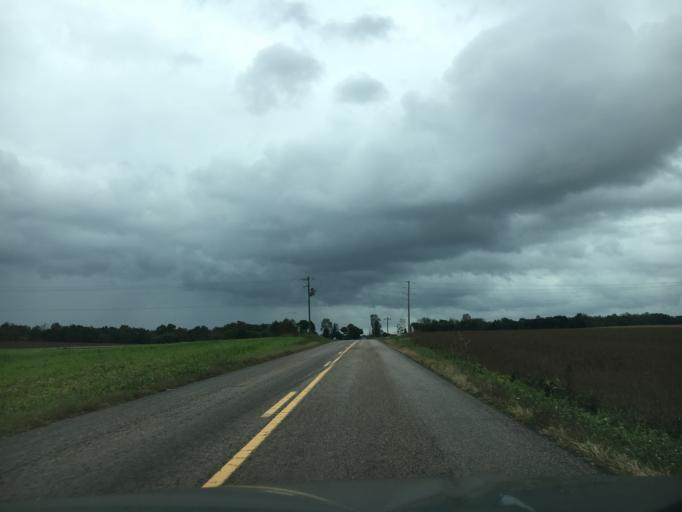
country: US
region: Virginia
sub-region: Amelia County
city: Amelia Court House
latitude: 37.4016
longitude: -77.9684
